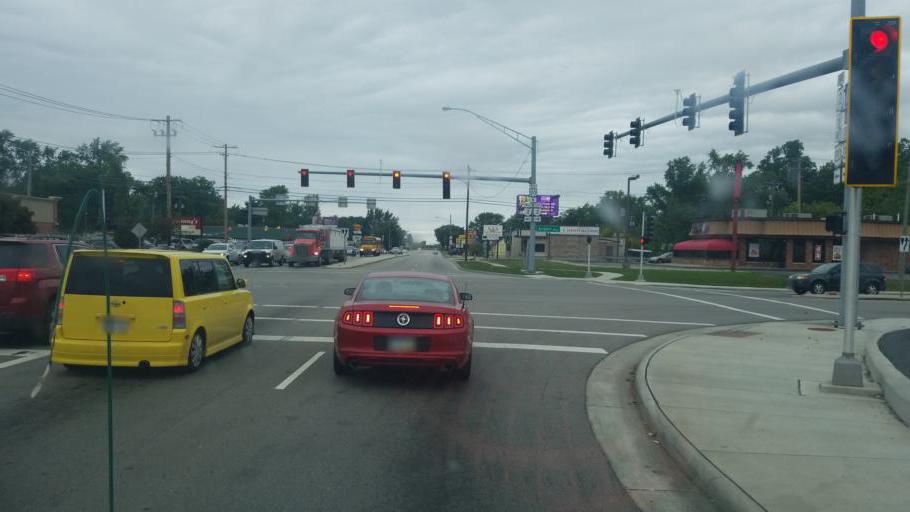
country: US
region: Ohio
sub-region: Lucas County
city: Holland
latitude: 41.6163
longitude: -83.6645
